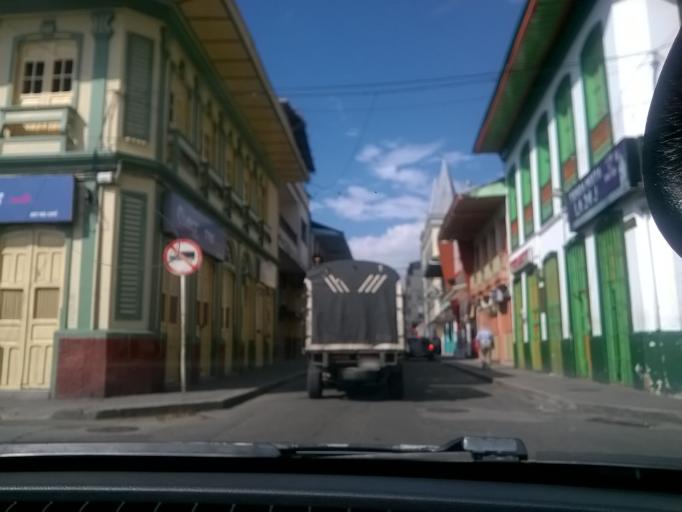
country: CO
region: Quindio
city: Calarca
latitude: 4.5296
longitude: -75.6405
